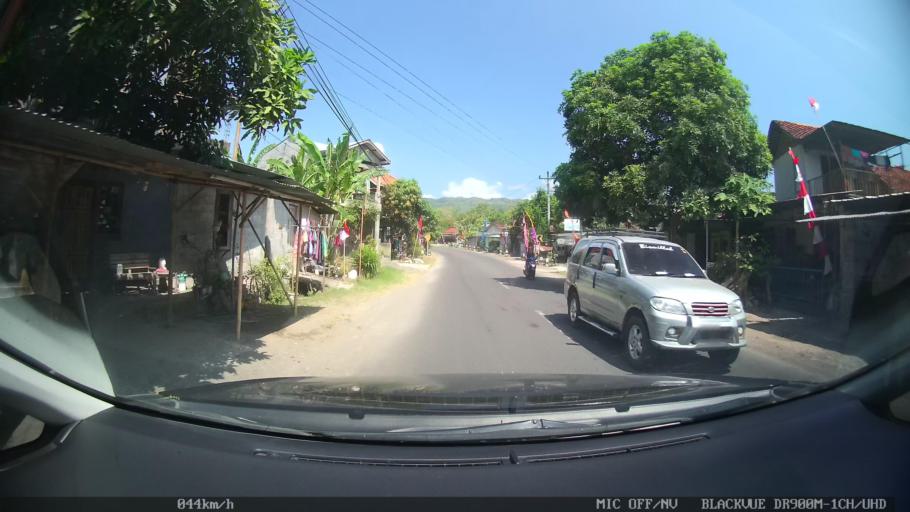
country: ID
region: Daerah Istimewa Yogyakarta
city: Pundong
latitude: -7.9505
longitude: 110.3780
